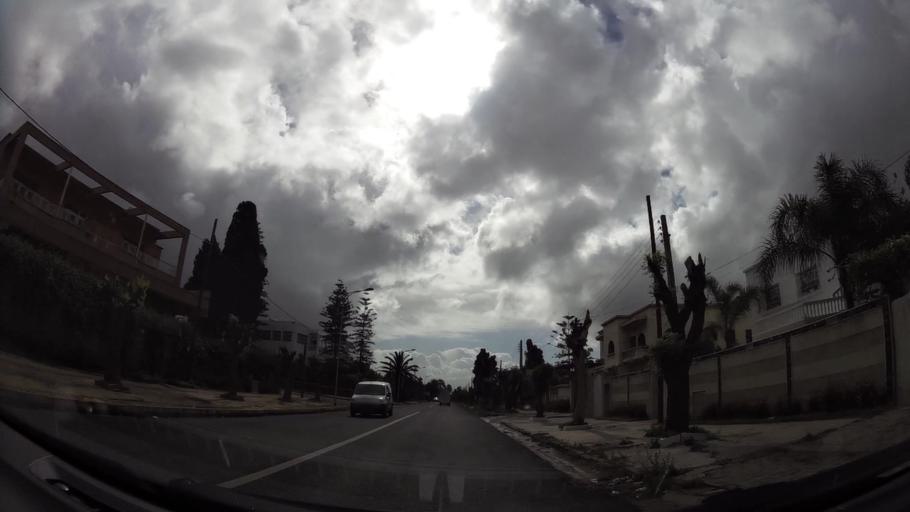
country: MA
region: Grand Casablanca
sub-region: Casablanca
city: Casablanca
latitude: 33.5534
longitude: -7.6152
